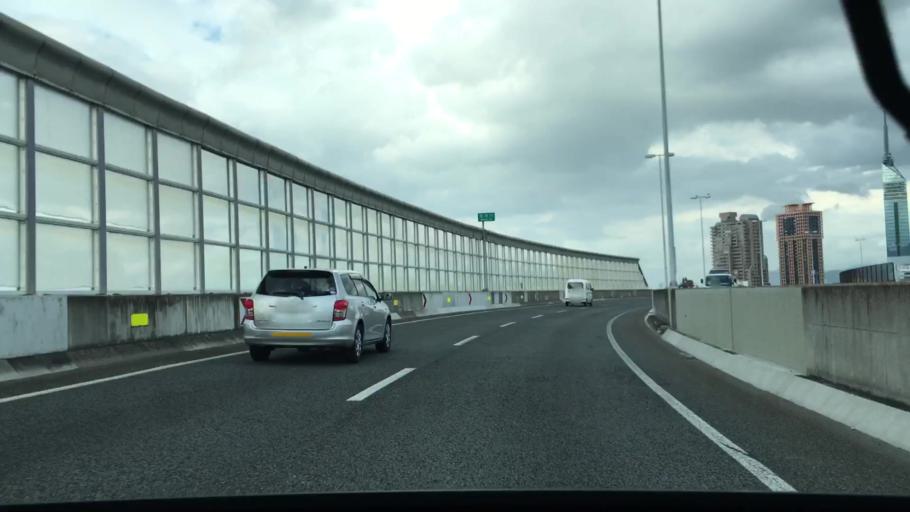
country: JP
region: Fukuoka
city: Fukuoka-shi
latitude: 33.5870
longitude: 130.3418
